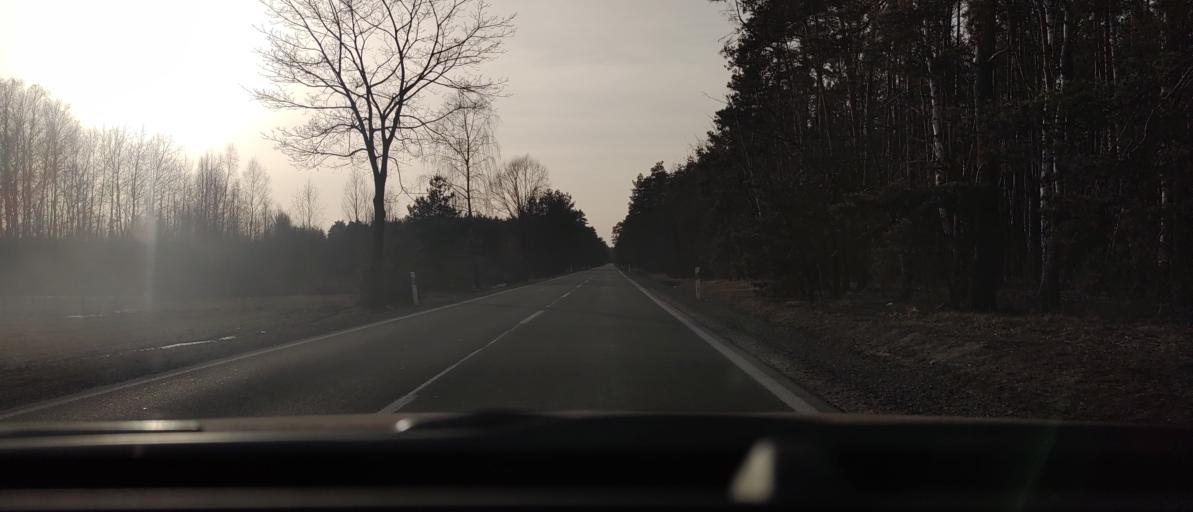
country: PL
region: Masovian Voivodeship
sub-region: Powiat bialobrzeski
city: Wysmierzyce
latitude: 51.6283
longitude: 20.8741
